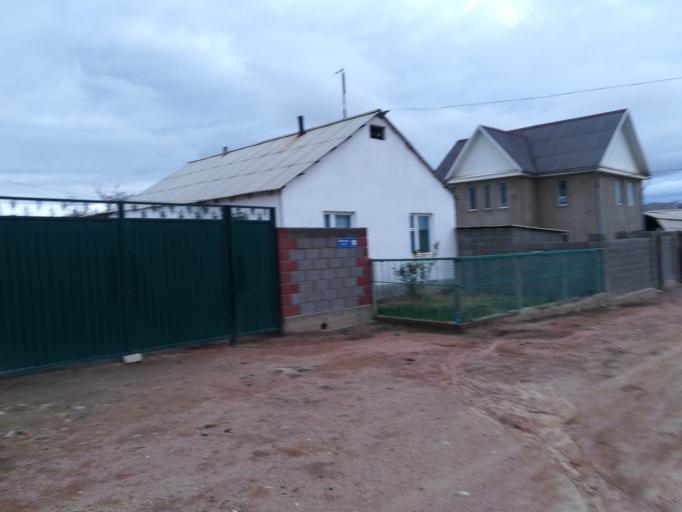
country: KG
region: Ysyk-Koel
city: Bokombayevskoye
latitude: 42.1143
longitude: 76.9819
